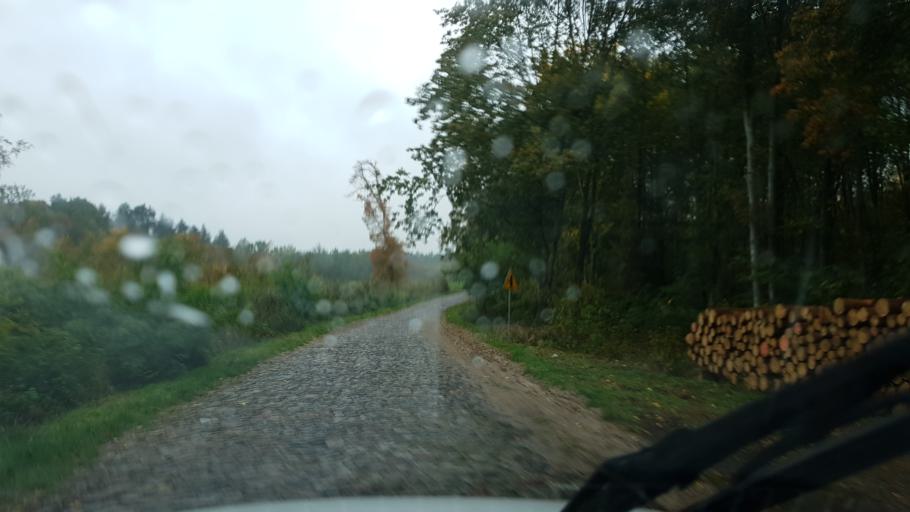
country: PL
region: West Pomeranian Voivodeship
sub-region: Powiat mysliborski
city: Barlinek
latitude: 53.0298
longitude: 15.2306
